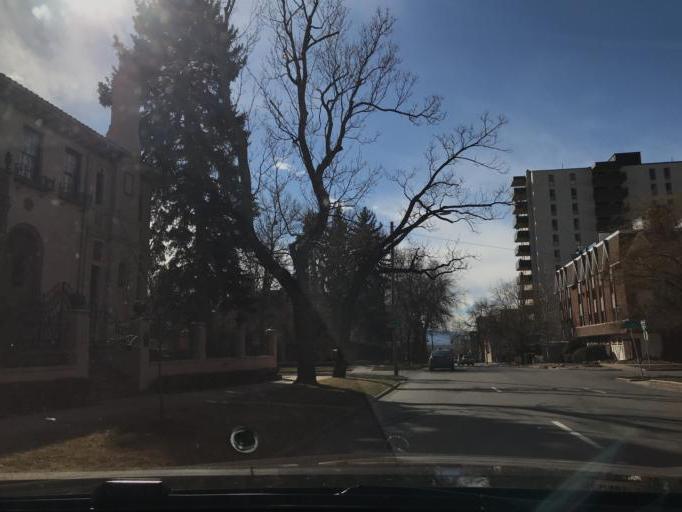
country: US
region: Colorado
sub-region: Denver County
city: Denver
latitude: 39.7290
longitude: -104.9806
